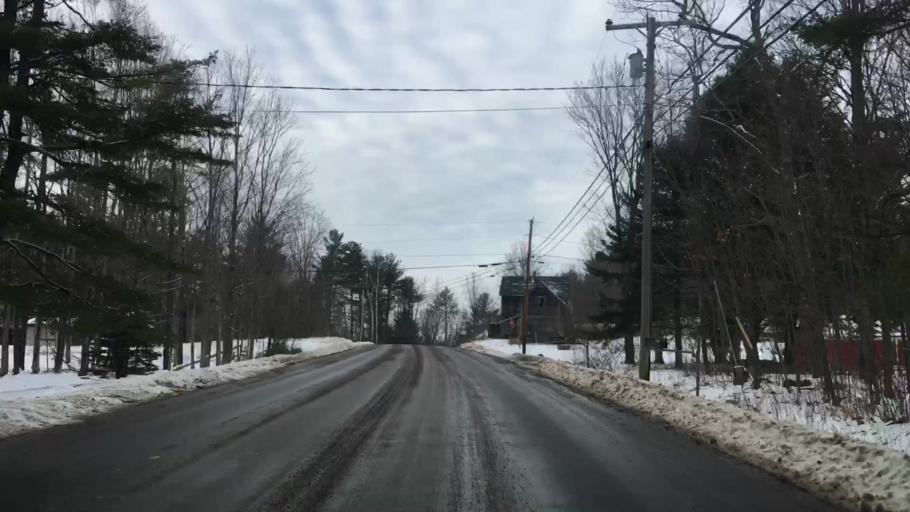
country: US
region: Maine
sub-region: Lincoln County
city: Whitefield
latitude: 44.2487
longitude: -69.6350
